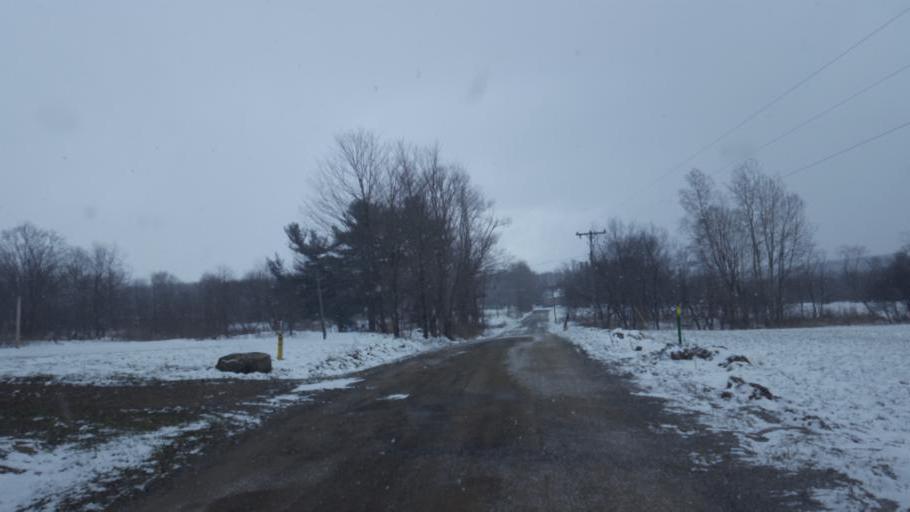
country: US
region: Pennsylvania
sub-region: Mercer County
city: Stoneboro
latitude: 41.4244
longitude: -80.0709
